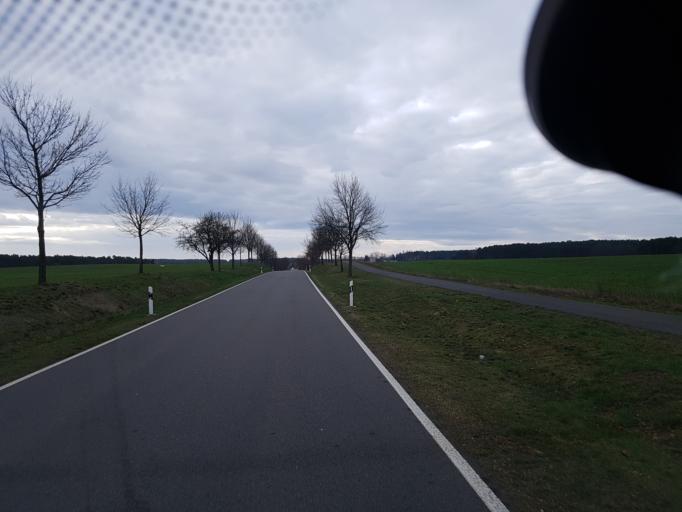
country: DE
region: Brandenburg
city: Gross Lindow
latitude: 52.1532
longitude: 14.5206
